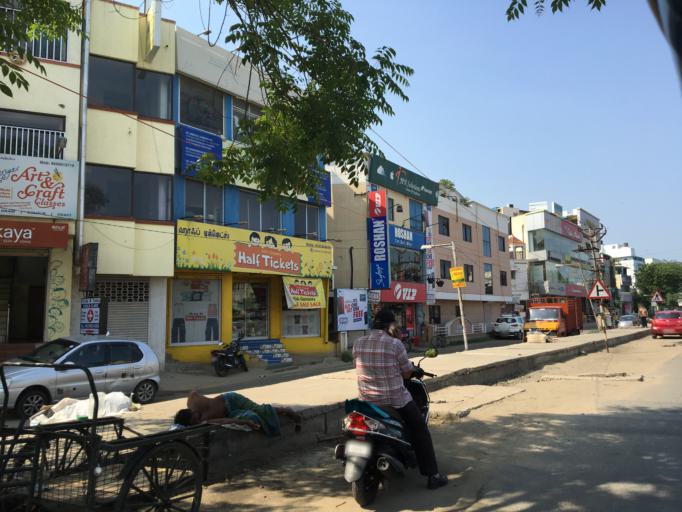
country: IN
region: Tamil Nadu
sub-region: Kancheepuram
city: Perungudi
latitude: 12.9778
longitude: 80.2241
